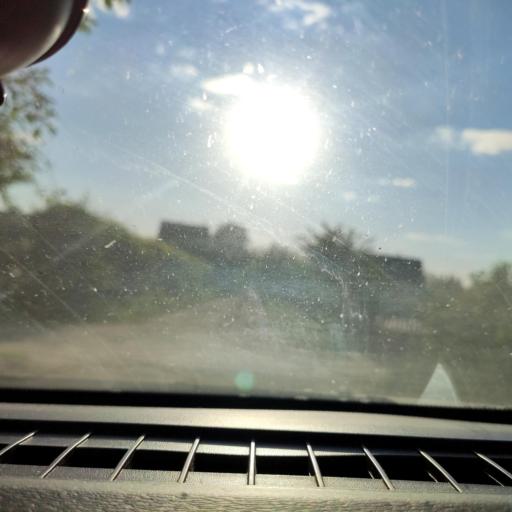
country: RU
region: Voronezj
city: Maslovka
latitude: 51.5204
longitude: 39.2315
